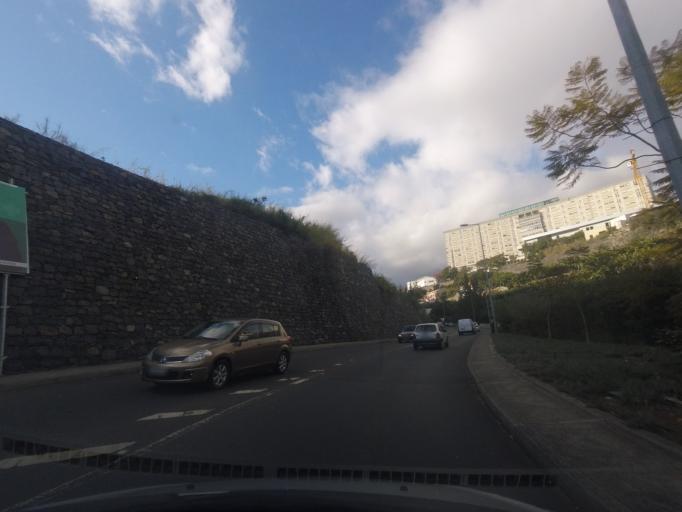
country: PT
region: Madeira
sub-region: Funchal
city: Funchal
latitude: 32.6466
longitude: -16.9243
